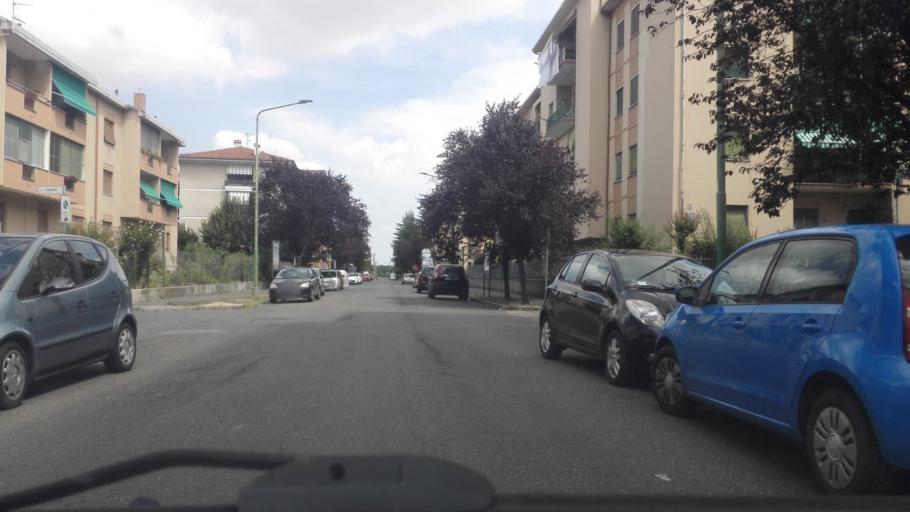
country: IT
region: Piedmont
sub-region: Provincia di Alessandria
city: Novi Ligure
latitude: 44.7685
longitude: 8.7907
